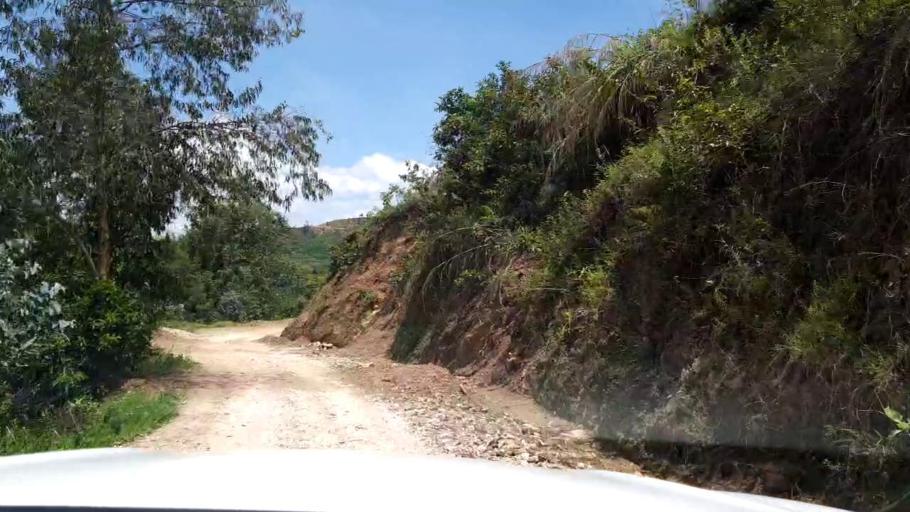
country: RW
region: Southern Province
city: Gitarama
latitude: -1.9839
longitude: 29.6211
